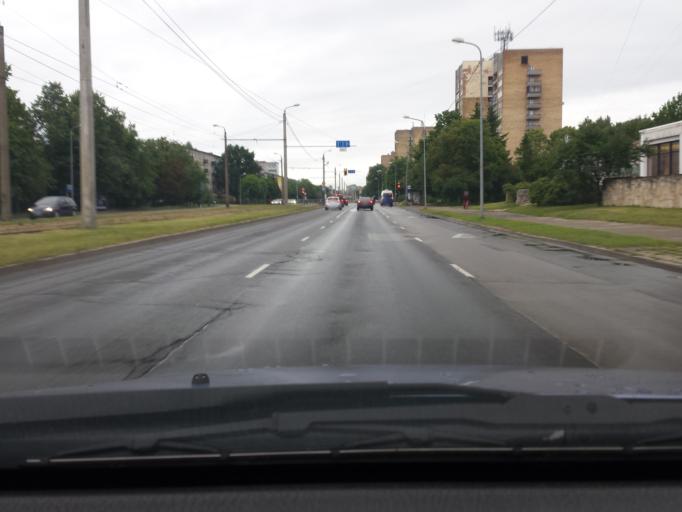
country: LV
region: Kekava
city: Balozi
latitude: 56.9137
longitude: 24.1764
